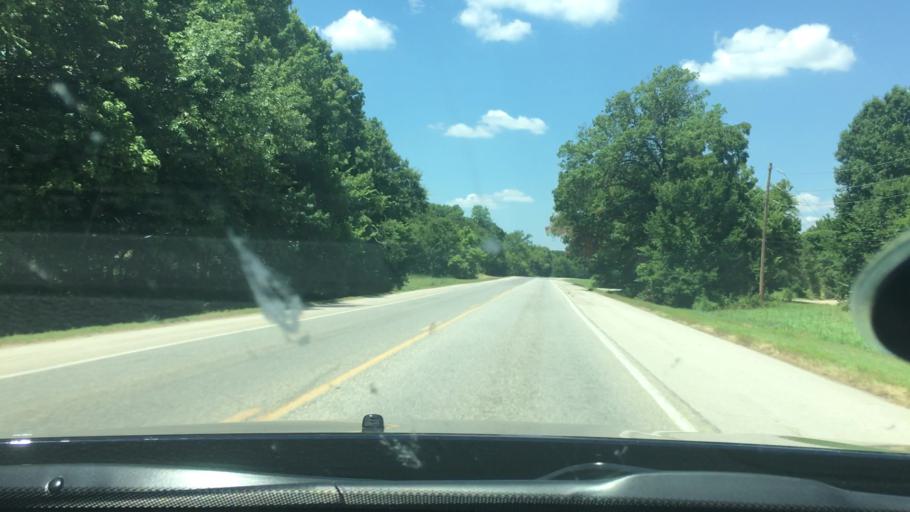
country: US
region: Oklahoma
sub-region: Marshall County
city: Oakland
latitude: 34.1735
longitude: -96.8488
